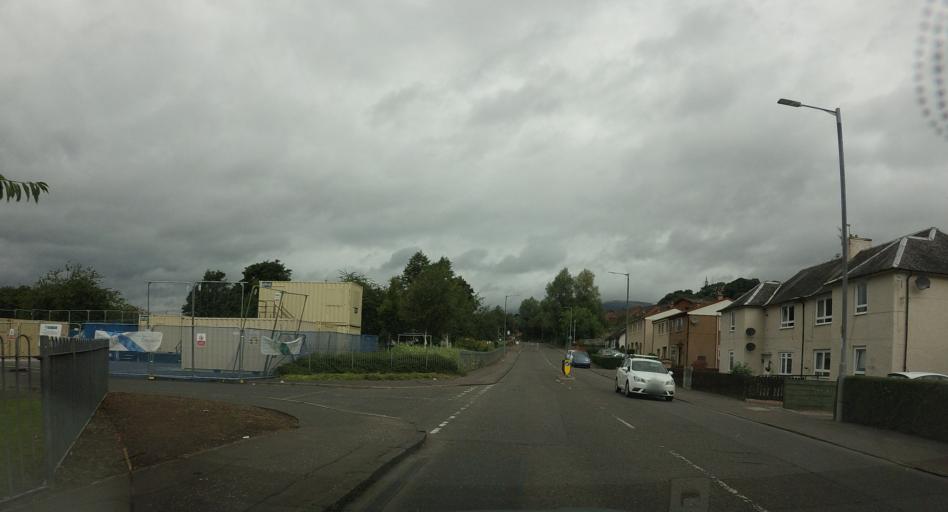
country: GB
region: Scotland
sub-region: Clackmannanshire
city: Alloa
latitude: 56.1282
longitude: -3.7871
